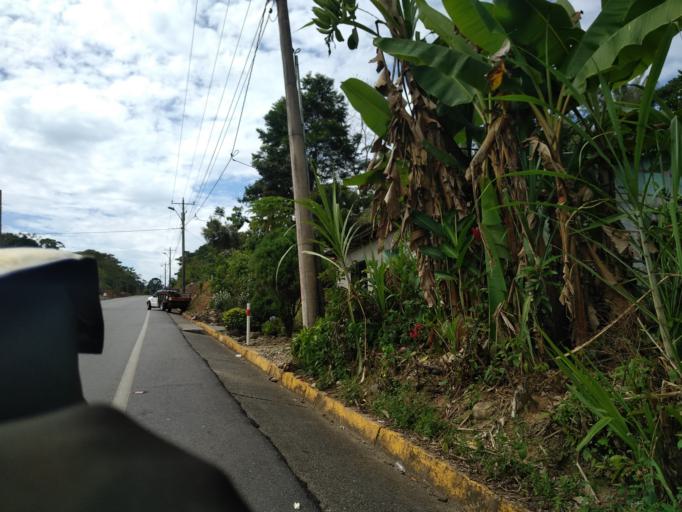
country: EC
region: Napo
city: Tena
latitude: -1.1213
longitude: -77.8104
